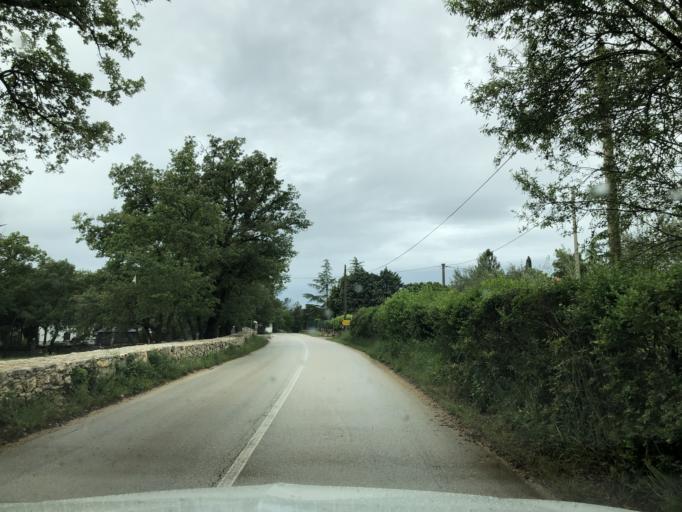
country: HR
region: Istarska
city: Buje
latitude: 45.4436
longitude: 13.6483
